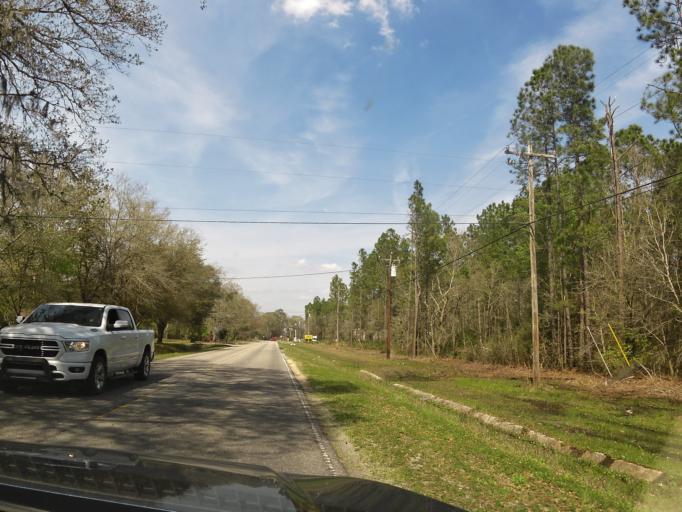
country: US
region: Florida
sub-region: Clay County
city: Middleburg
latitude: 30.1107
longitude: -81.8647
